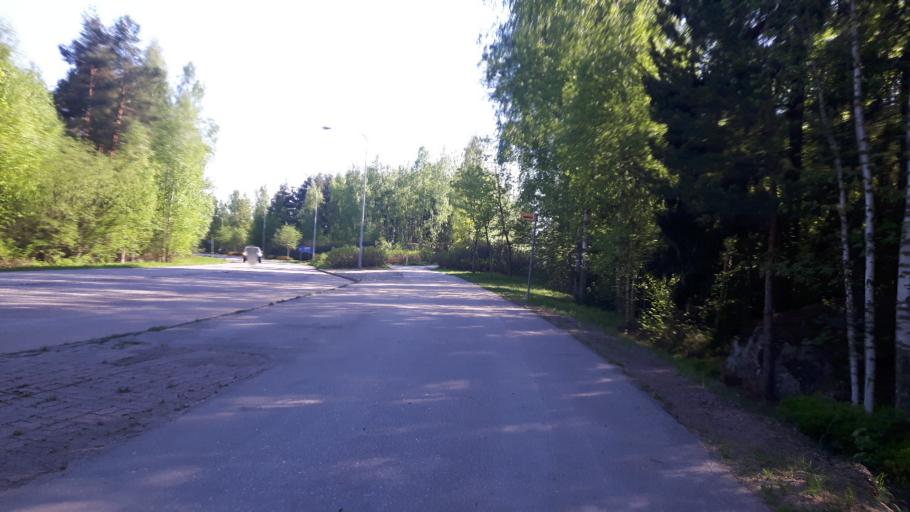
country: FI
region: Kymenlaakso
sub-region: Kotka-Hamina
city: Kotka
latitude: 60.4377
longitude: 26.8817
